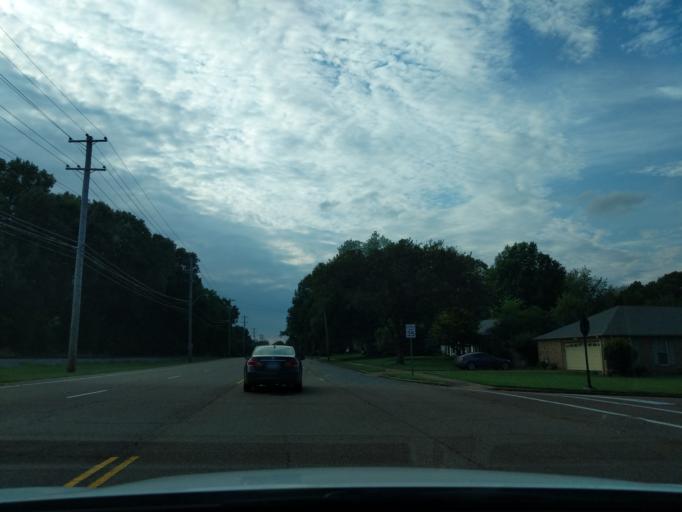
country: US
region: Tennessee
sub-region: Shelby County
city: Germantown
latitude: 35.0761
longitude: -89.7967
